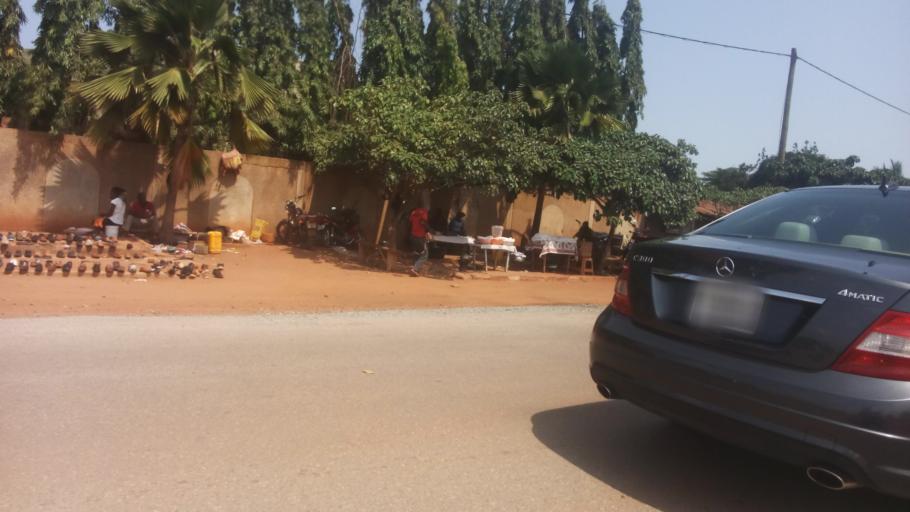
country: TG
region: Maritime
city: Lome
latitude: 6.1946
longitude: 1.2386
